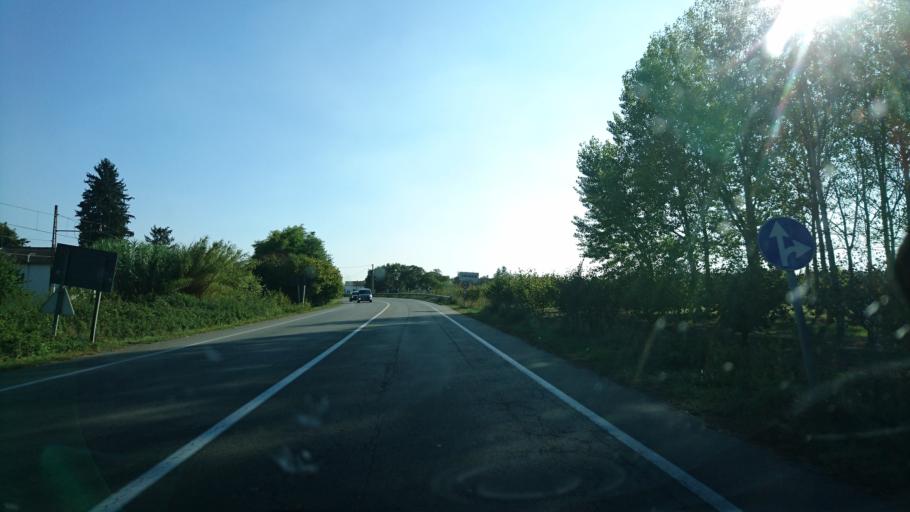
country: IT
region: Piedmont
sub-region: Provincia di Alessandria
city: Gamalero
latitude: 44.7818
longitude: 8.5370
